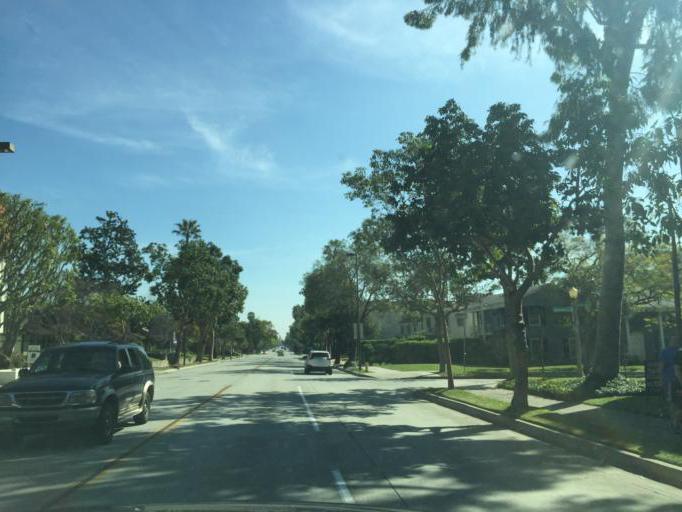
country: US
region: California
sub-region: Los Angeles County
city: Pasadena
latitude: 34.1358
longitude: -118.1448
